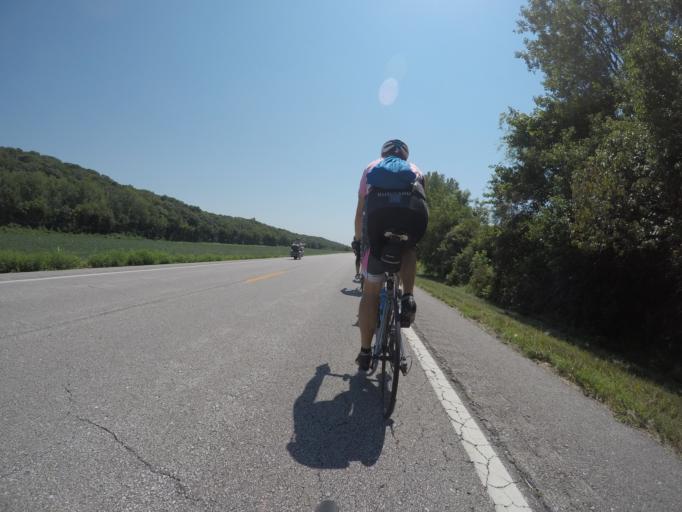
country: US
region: Kansas
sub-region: Leavenworth County
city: Leavenworth
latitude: 39.3473
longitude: -94.8646
